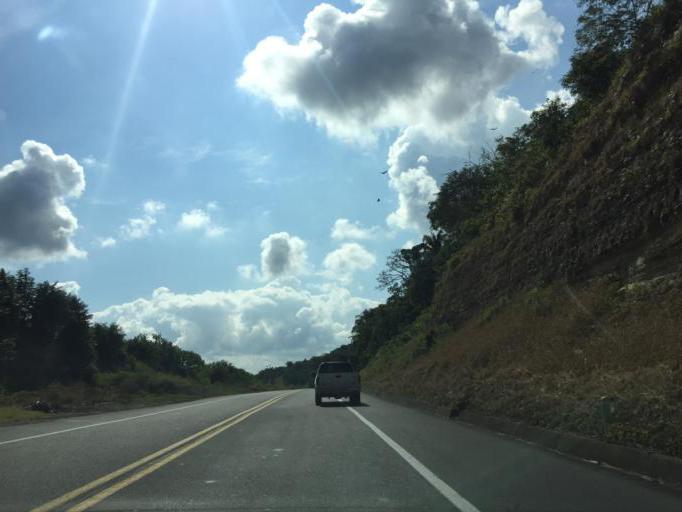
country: MX
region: Veracruz
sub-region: Papantla
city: Residencial Tajin
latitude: 20.6604
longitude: -97.4431
